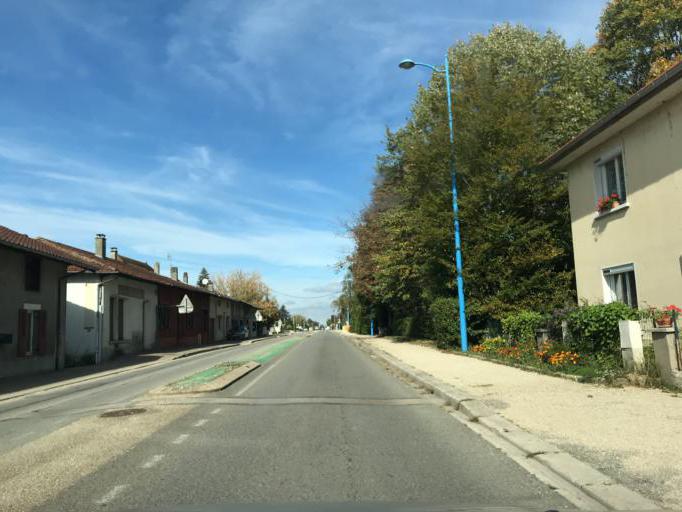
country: FR
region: Rhone-Alpes
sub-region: Departement de l'Ain
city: Montrevel-en-Bresse
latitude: 46.3406
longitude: 5.1276
